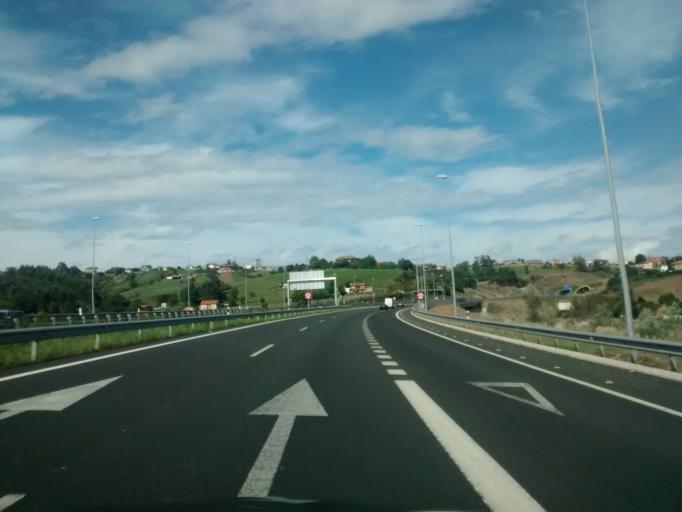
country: ES
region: Cantabria
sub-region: Provincia de Cantabria
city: Camargo
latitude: 43.3865
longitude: -3.8622
